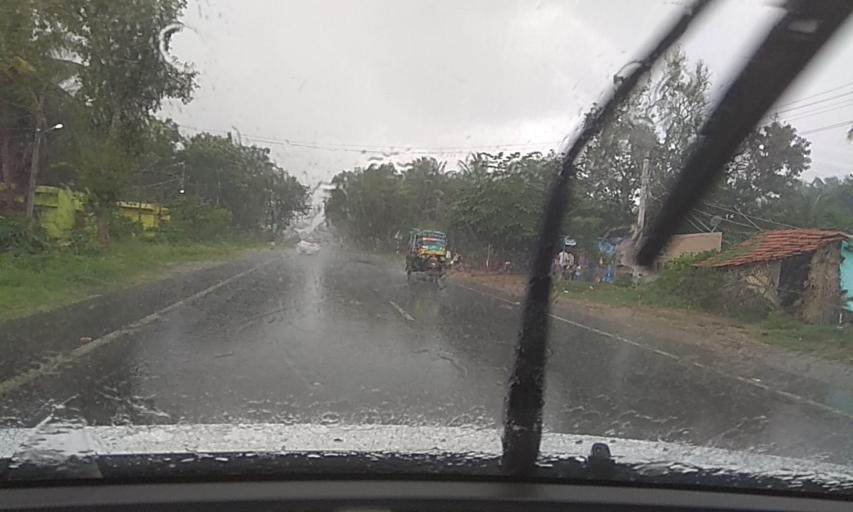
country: IN
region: Karnataka
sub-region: Tumkur
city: Kunigal
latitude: 13.0041
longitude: 77.0225
